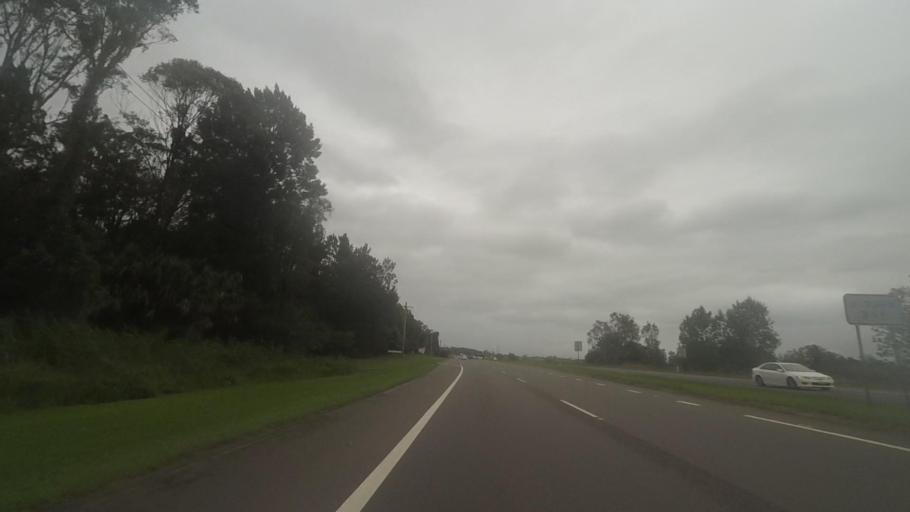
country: AU
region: New South Wales
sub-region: Port Stephens Shire
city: Raymond Terrace
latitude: -32.8003
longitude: 151.7165
